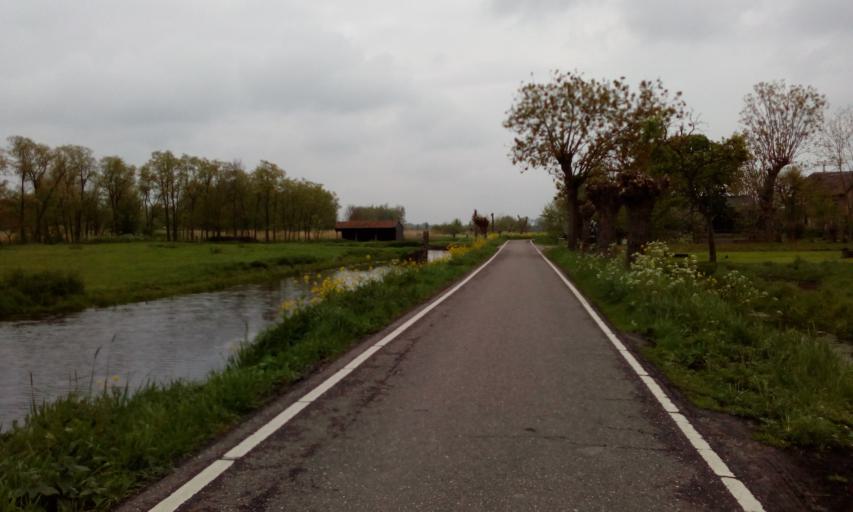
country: NL
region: South Holland
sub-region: Gemeente Schiedam
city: Schiedam
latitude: 51.9490
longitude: 4.3617
